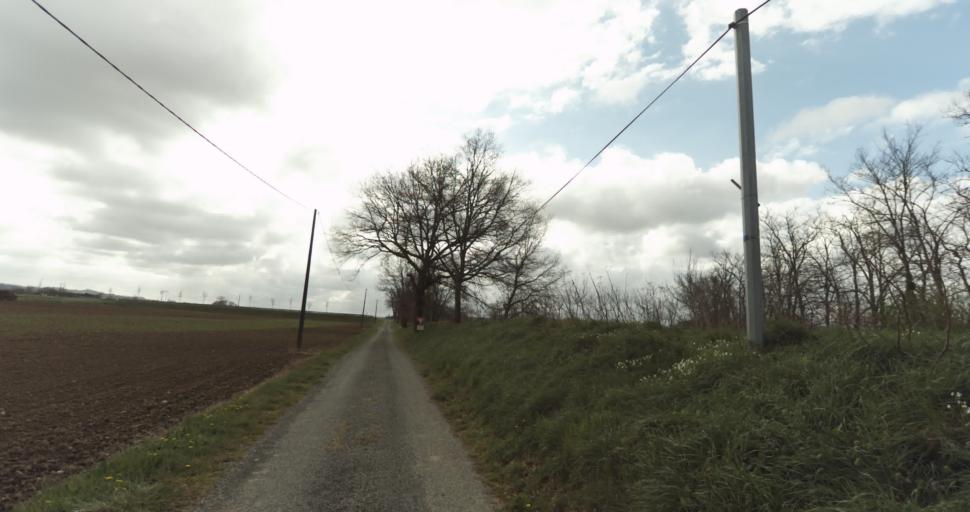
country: FR
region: Midi-Pyrenees
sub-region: Departement de la Haute-Garonne
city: Miremont
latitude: 43.3475
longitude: 1.4432
